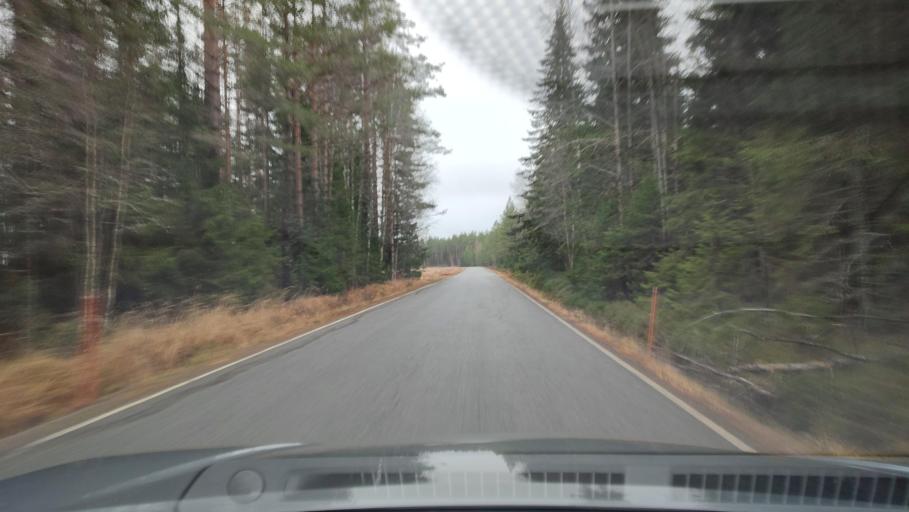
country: FI
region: Southern Ostrobothnia
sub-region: Suupohja
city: Isojoki
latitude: 62.1739
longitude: 21.9007
